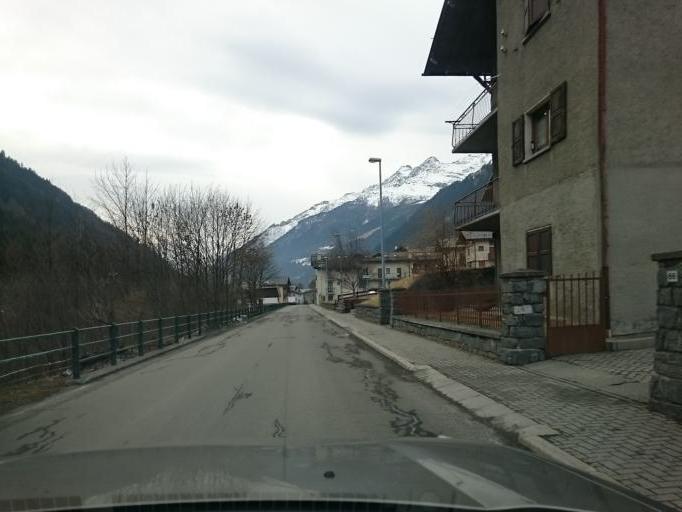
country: IT
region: Lombardy
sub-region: Provincia di Sondrio
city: Valdisotto
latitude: 46.4331
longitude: 10.3574
